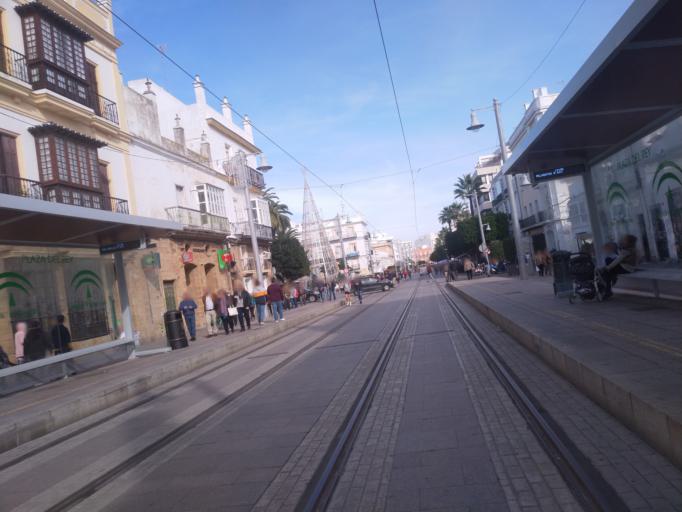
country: ES
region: Andalusia
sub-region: Provincia de Cadiz
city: San Fernando
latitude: 36.4639
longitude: -6.1984
